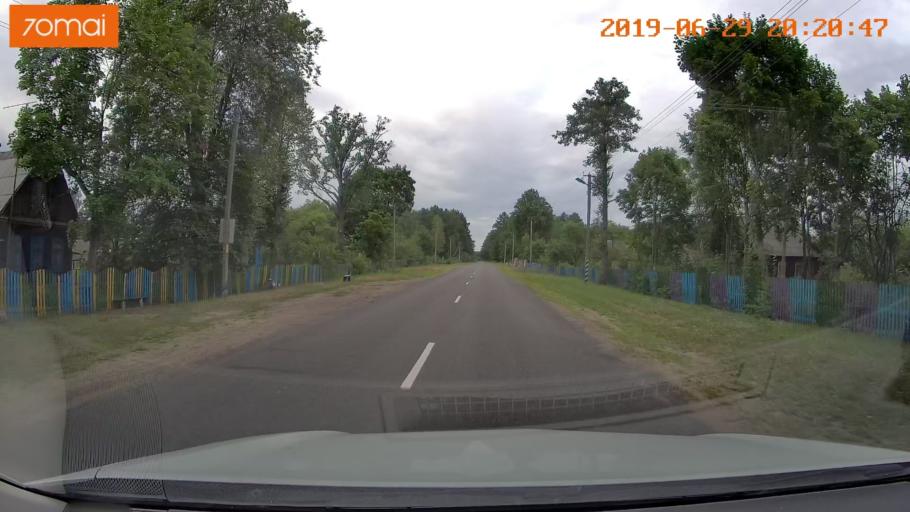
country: BY
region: Brest
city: Asnyezhytsy
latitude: 52.4135
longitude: 26.2505
